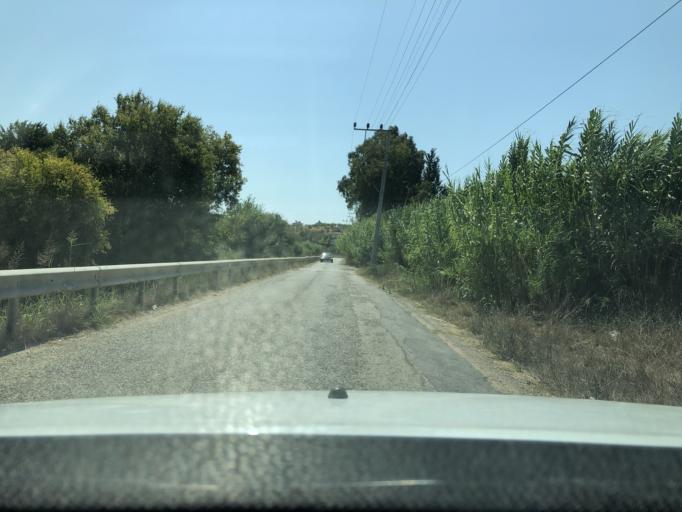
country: TR
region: Antalya
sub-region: Manavgat
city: Manavgat
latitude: 36.8045
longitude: 31.4674
